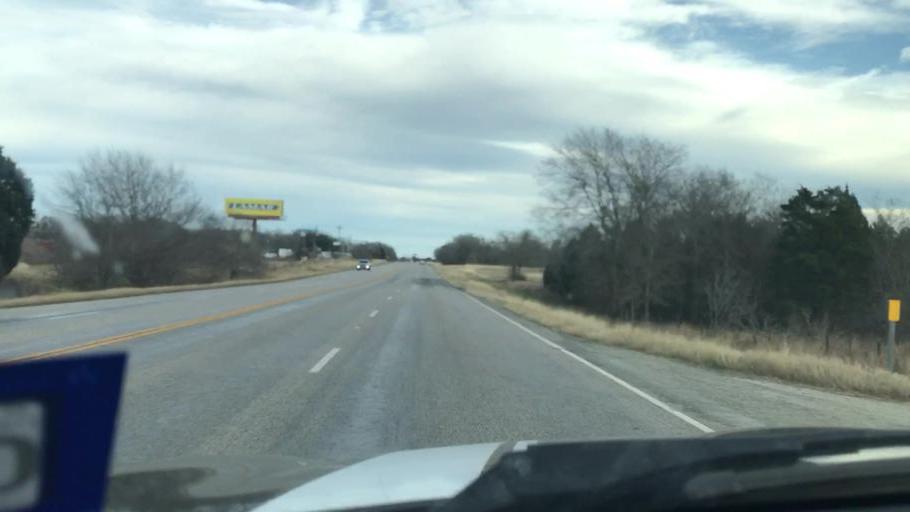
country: US
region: Texas
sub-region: Bastrop County
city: Elgin
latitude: 30.2968
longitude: -97.2787
